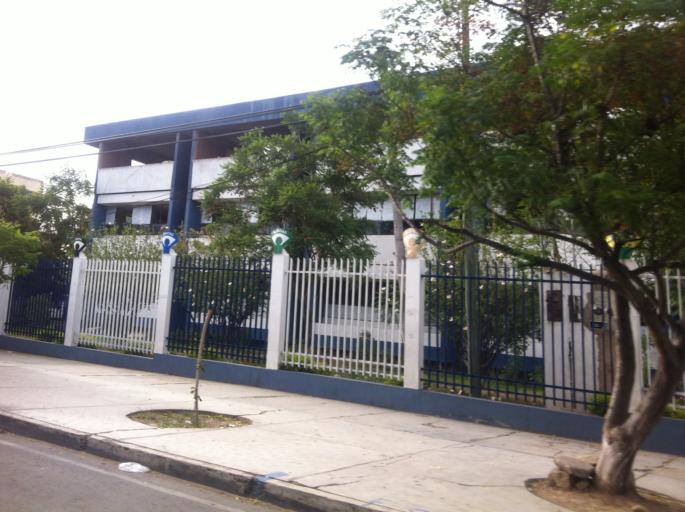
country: BO
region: Cochabamba
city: Cochabamba
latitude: -17.3801
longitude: -66.1460
